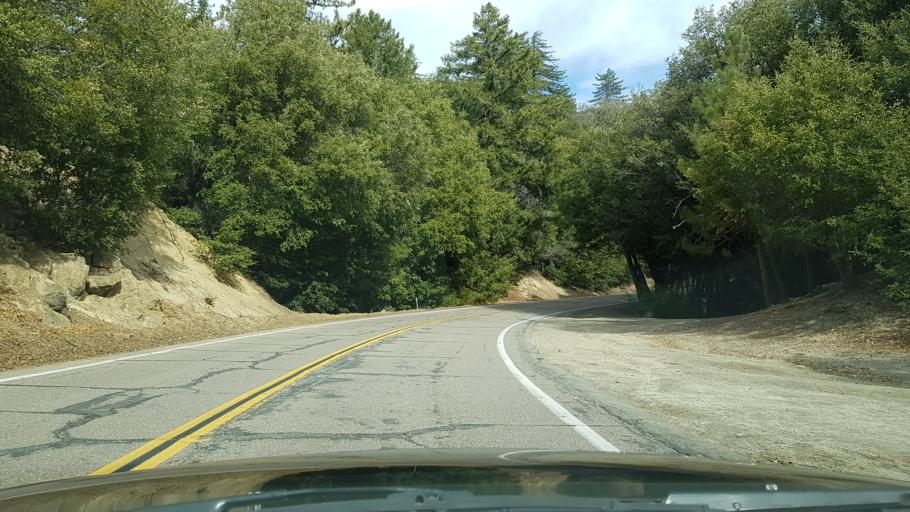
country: US
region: California
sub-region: Riverside County
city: Aguanga
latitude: 33.3447
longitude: -116.8799
